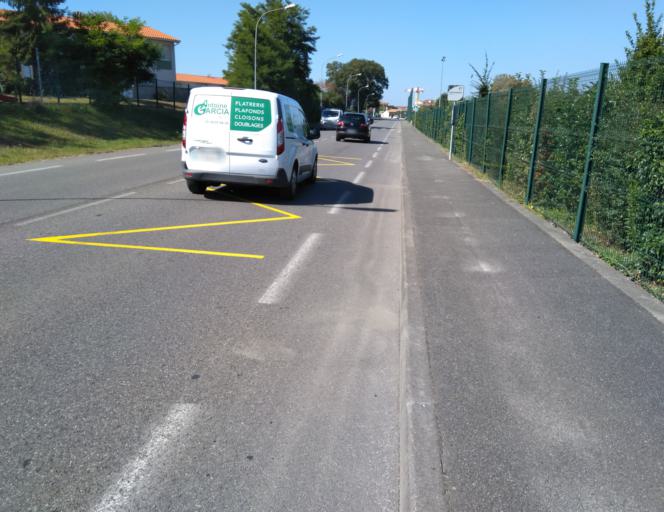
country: FR
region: Aquitaine
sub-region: Departement des Landes
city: Dax
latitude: 43.7007
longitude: -1.0385
